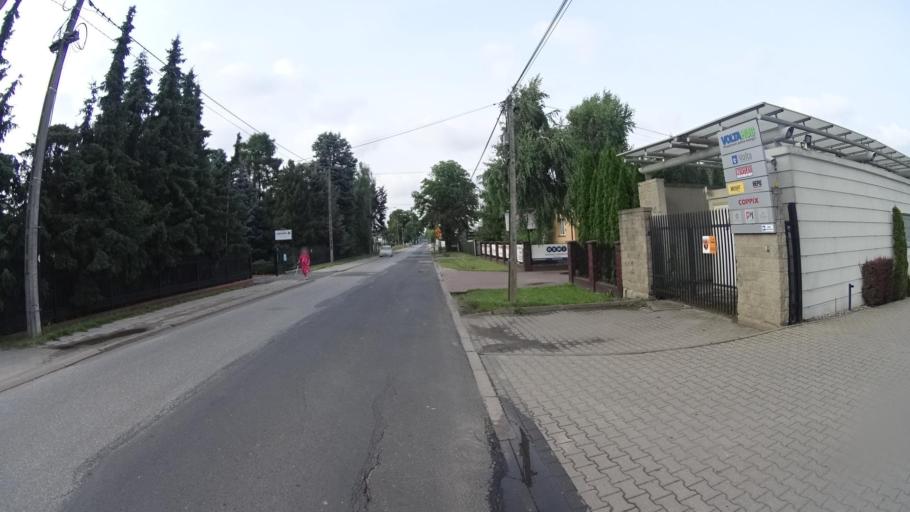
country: PL
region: Masovian Voivodeship
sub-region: Warszawa
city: Wlochy
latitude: 52.1895
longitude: 20.9268
